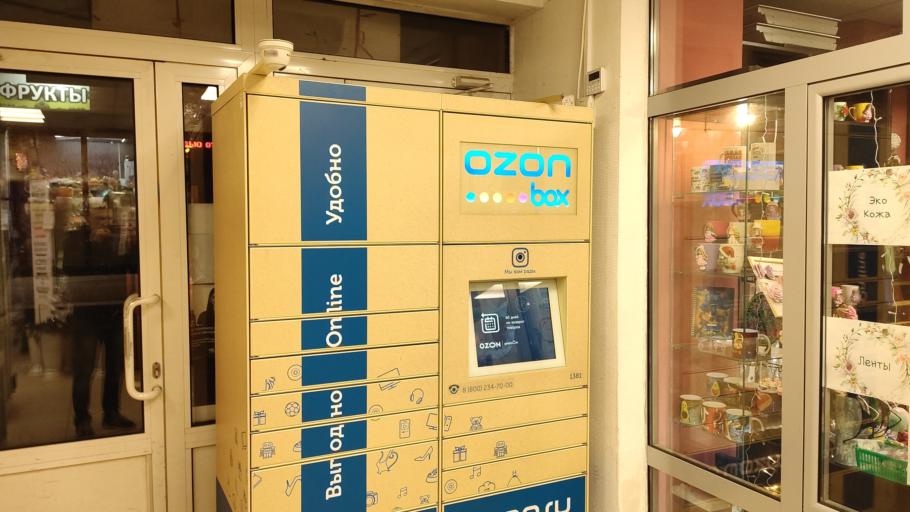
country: RU
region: Krasnodarskiy
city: Krasnodar
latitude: 45.0820
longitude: 39.0017
